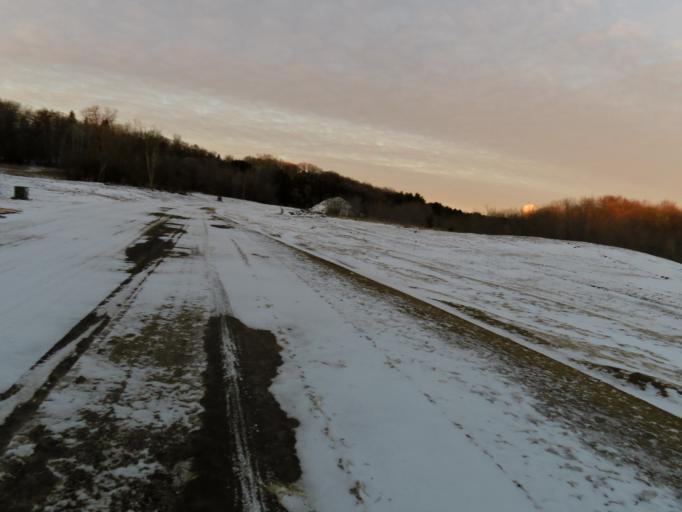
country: US
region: Minnesota
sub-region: Washington County
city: Lakeland
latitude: 44.9649
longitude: -92.8156
